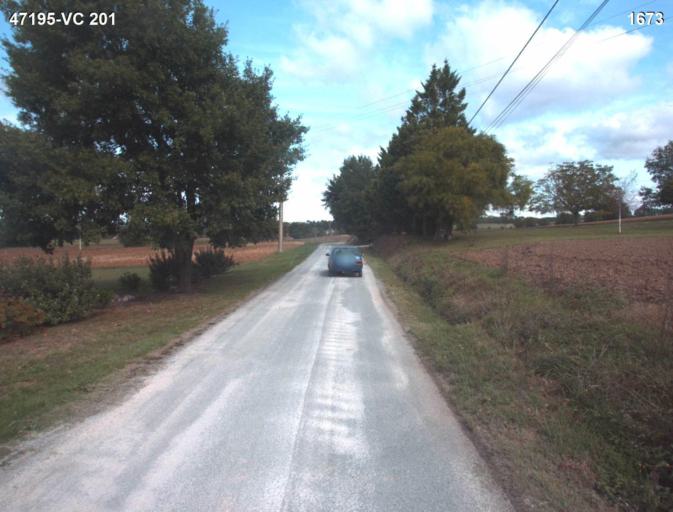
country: FR
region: Aquitaine
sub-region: Departement du Lot-et-Garonne
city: Barbaste
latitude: 44.1315
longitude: 0.2991
